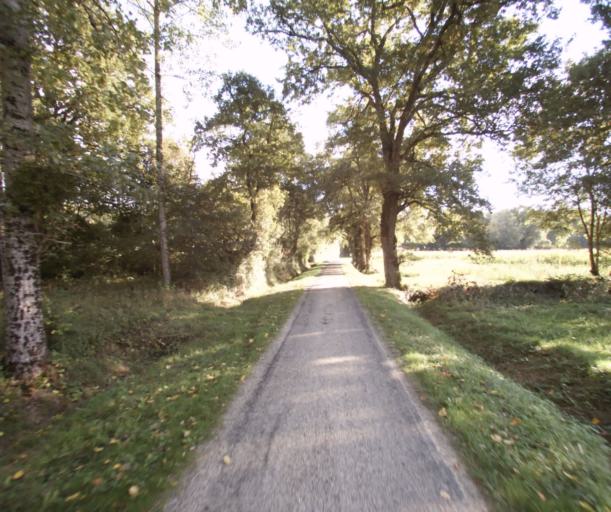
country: FR
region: Midi-Pyrenees
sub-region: Departement du Gers
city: Eauze
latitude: 43.8547
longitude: 0.0324
